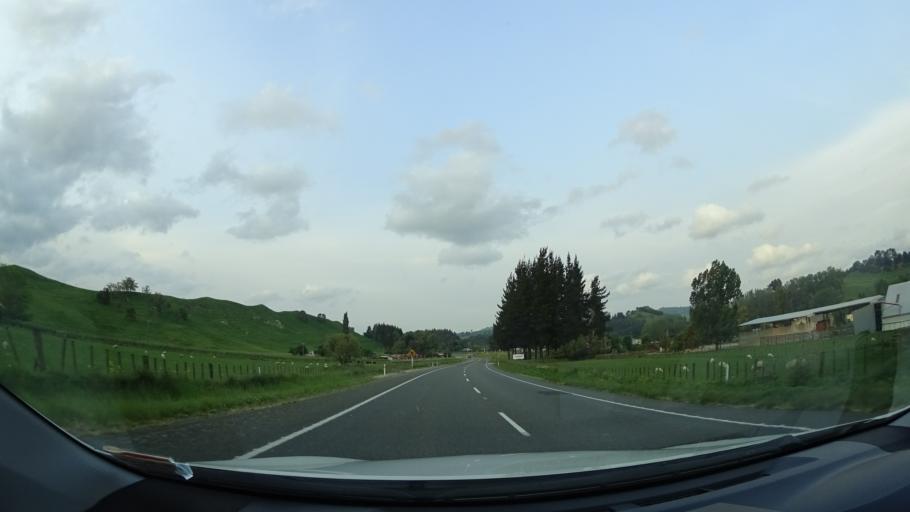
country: NZ
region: Manawatu-Wanganui
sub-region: Ruapehu District
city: Waiouru
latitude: -39.7366
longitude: 175.8412
